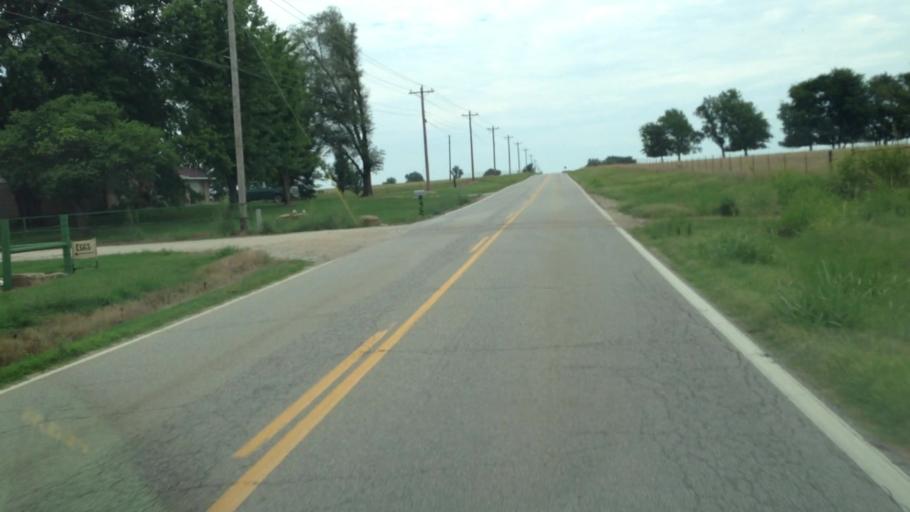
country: US
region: Oklahoma
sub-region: Delaware County
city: Cleora
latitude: 36.6051
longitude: -94.9634
